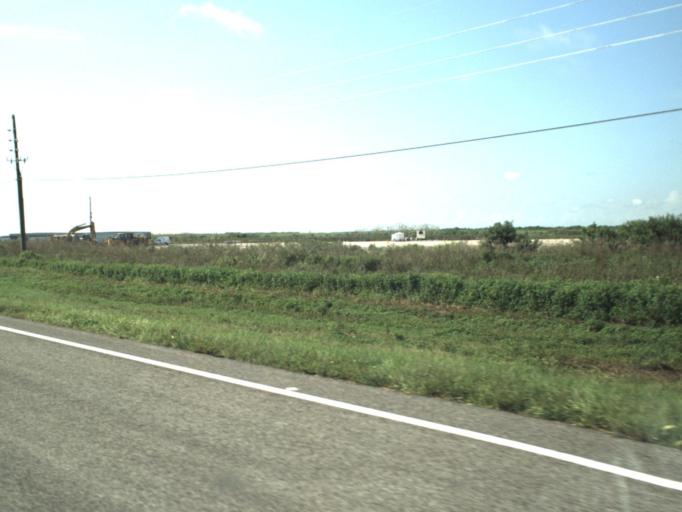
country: US
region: Florida
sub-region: Palm Beach County
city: Belle Glade Camp
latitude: 26.4874
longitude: -80.6561
